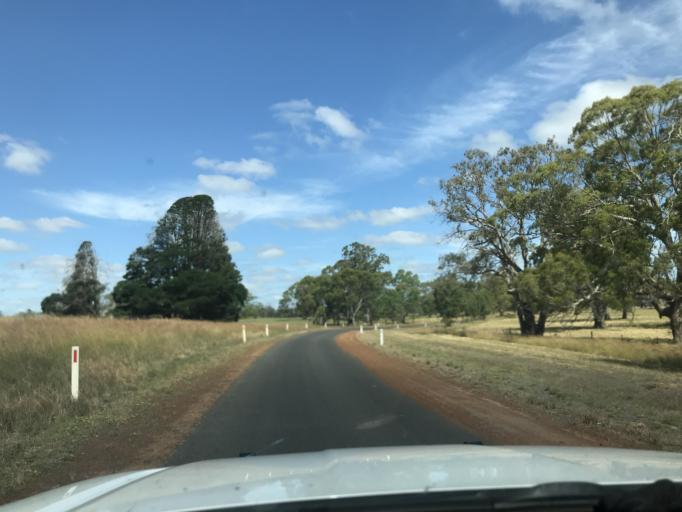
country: AU
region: South Australia
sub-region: Naracoorte and Lucindale
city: Naracoorte
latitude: -36.8655
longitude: 141.1737
